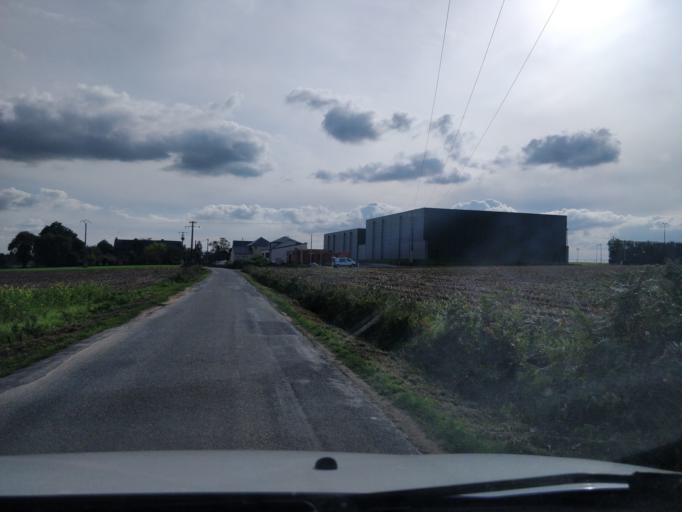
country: FR
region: Brittany
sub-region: Departement d'Ille-et-Vilaine
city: Chateaubourg
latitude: 48.1178
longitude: -1.3815
